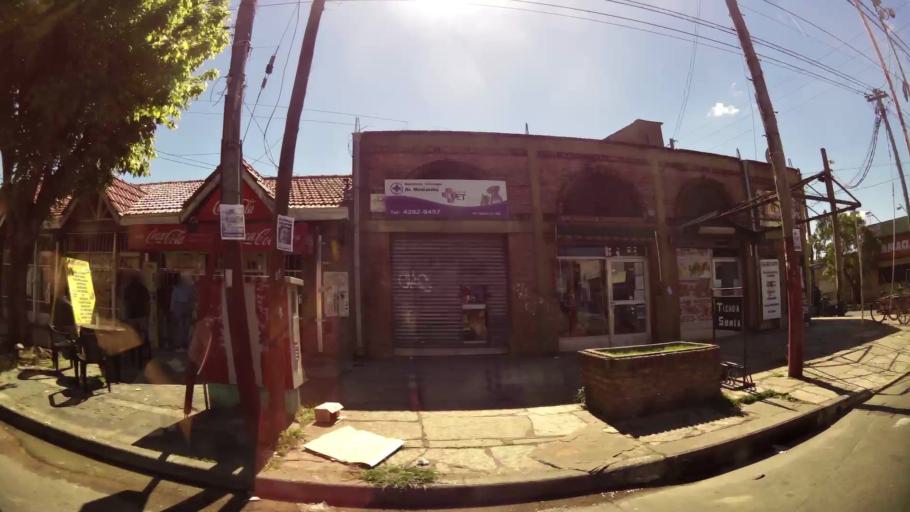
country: AR
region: Buenos Aires
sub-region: Partido de Lomas de Zamora
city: Lomas de Zamora
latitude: -34.7543
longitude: -58.4208
